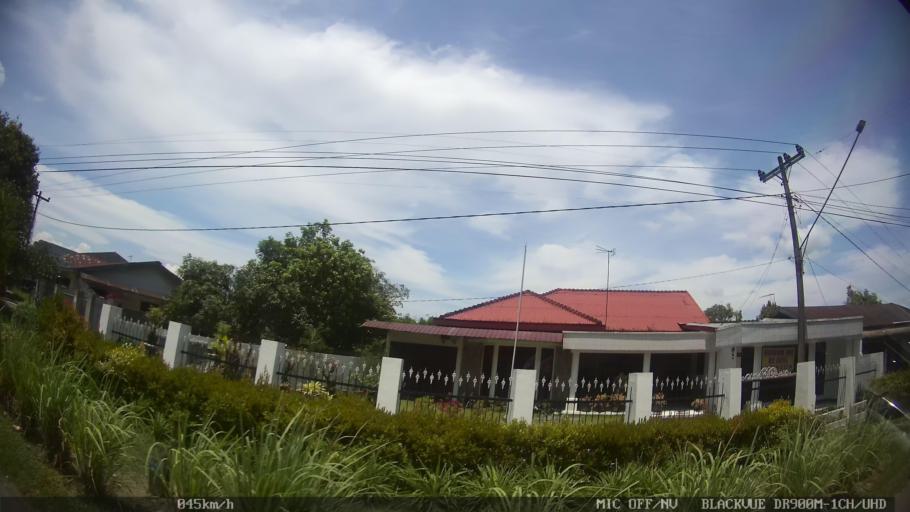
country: ID
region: North Sumatra
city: Binjai
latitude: 3.5926
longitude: 98.5032
